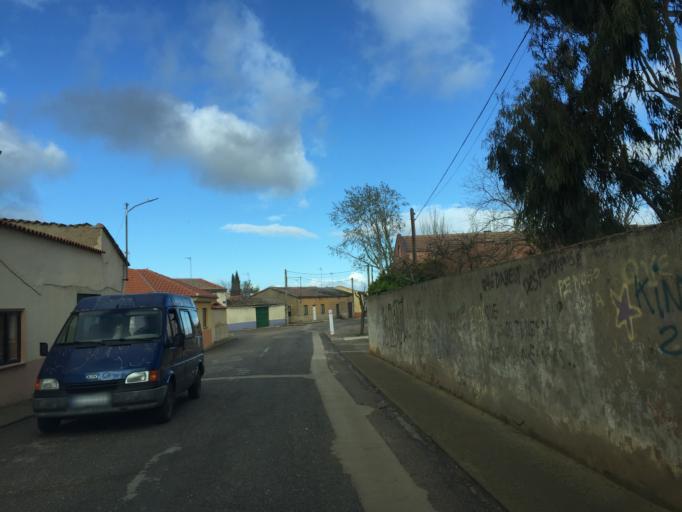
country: ES
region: Castille and Leon
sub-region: Provincia de Zamora
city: Manganeses de la Lampreana
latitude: 41.7521
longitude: -5.7128
